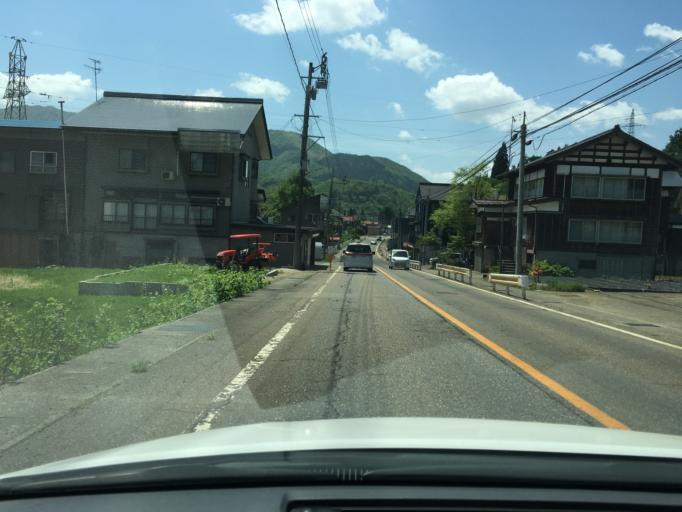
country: JP
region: Niigata
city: Tochio-honcho
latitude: 37.3150
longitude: 139.0142
